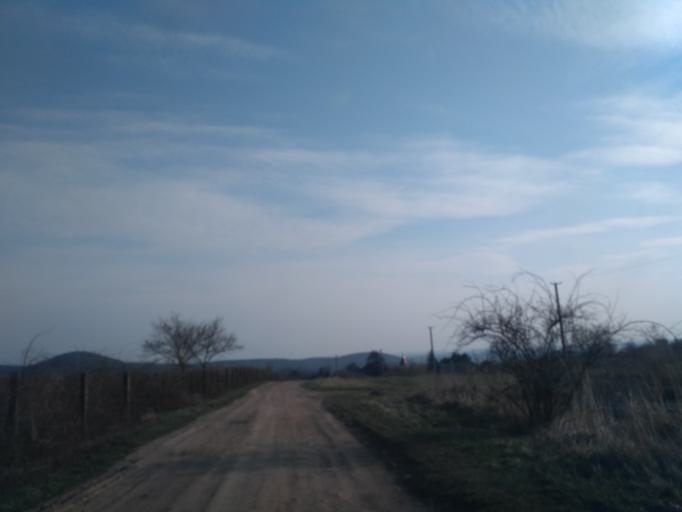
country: HU
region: Borsod-Abauj-Zemplen
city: Satoraljaujhely
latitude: 48.4318
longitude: 21.7169
